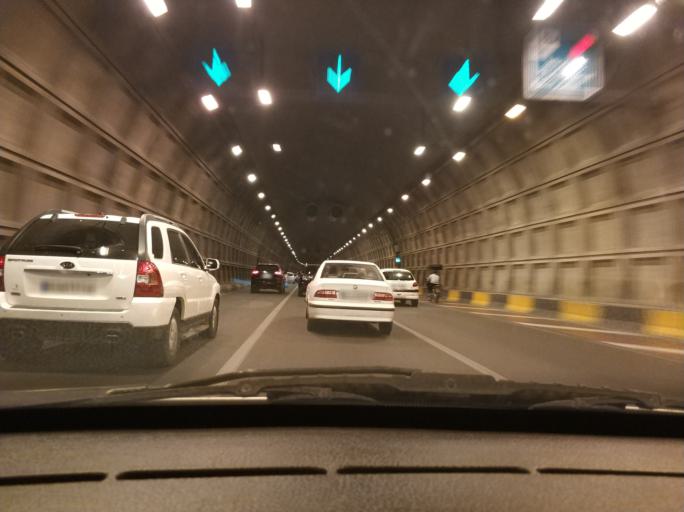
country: IR
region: Tehran
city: Tehran
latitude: 35.7435
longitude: 51.4079
